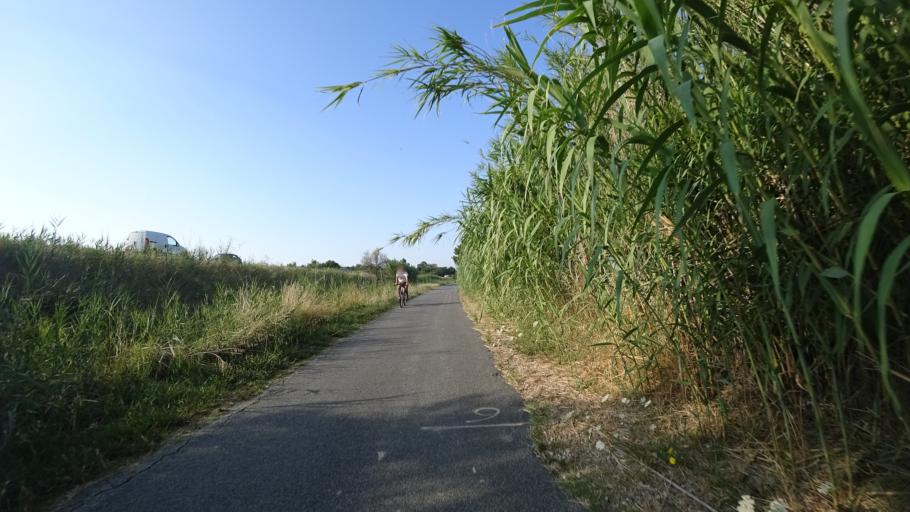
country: FR
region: Languedoc-Roussillon
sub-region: Departement des Pyrenees-Orientales
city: Sainte-Marie-Plage
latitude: 42.7224
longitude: 3.0296
